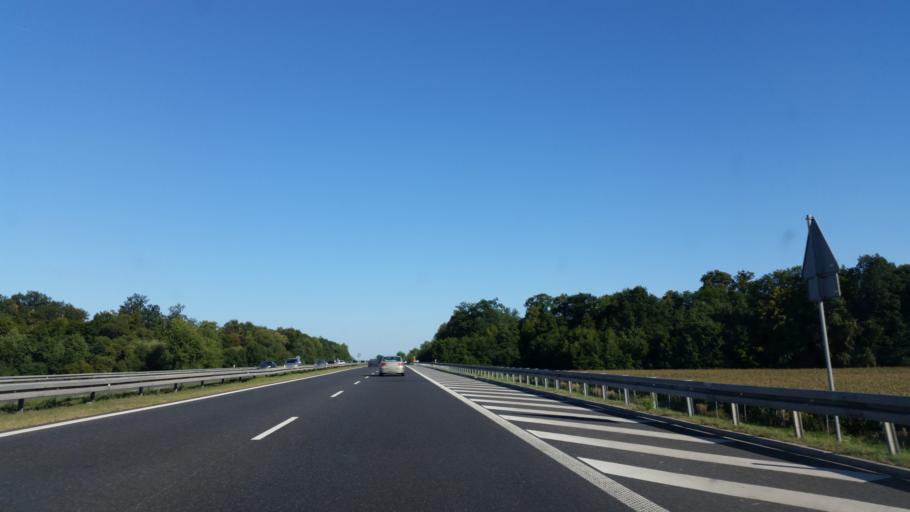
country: PL
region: Opole Voivodeship
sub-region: Powiat brzeski
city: Olszanka
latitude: 50.7308
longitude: 17.5057
